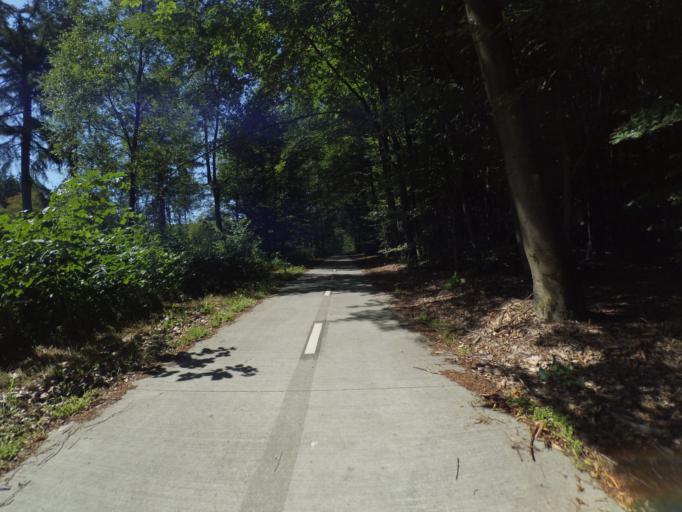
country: NL
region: Drenthe
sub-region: Gemeente Borger-Odoorn
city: Borger
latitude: 52.8948
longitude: 6.6584
